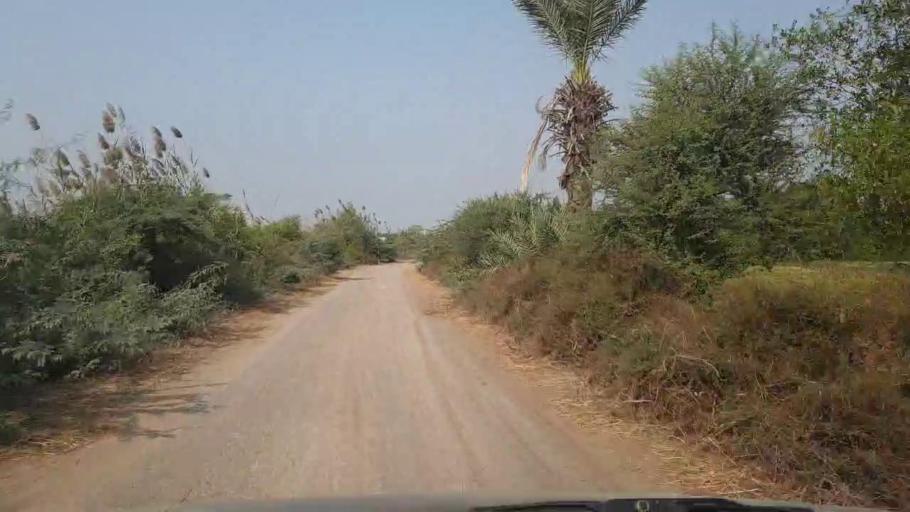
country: PK
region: Sindh
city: Tando Muhammad Khan
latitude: 25.0937
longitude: 68.3385
